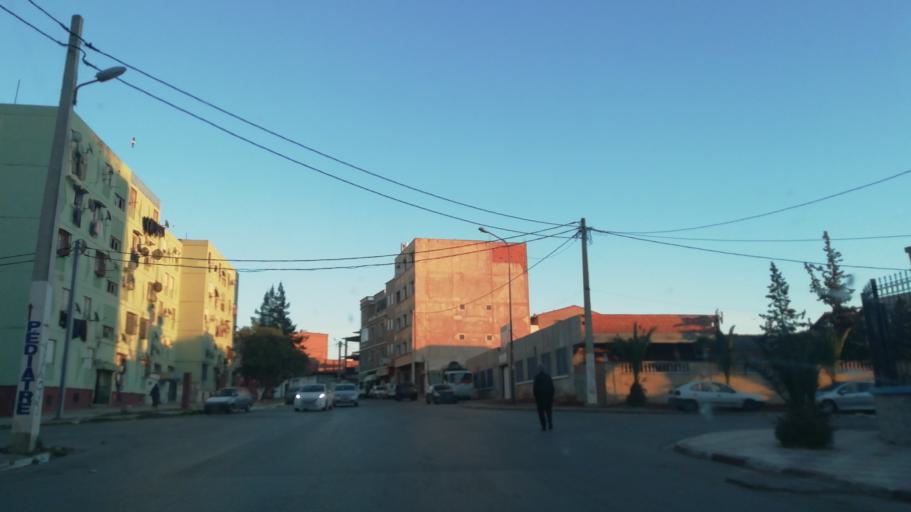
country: DZ
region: Oran
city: Oran
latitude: 35.6991
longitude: -0.5975
